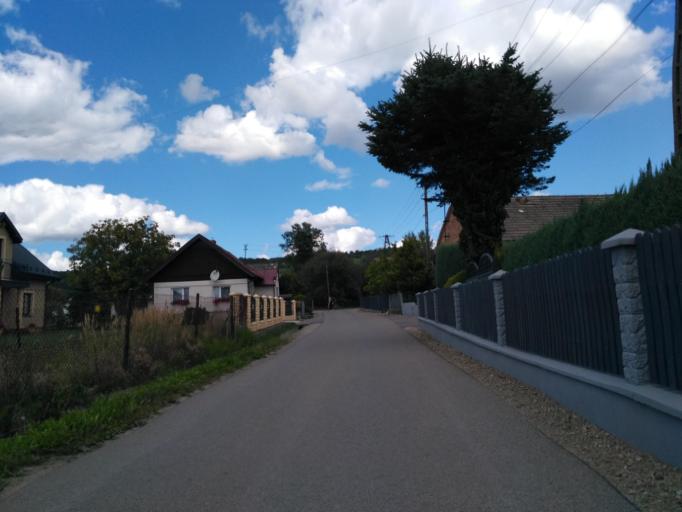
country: PL
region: Subcarpathian Voivodeship
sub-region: Powiat jasielski
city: Tarnowiec
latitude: 49.7650
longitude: 21.5314
